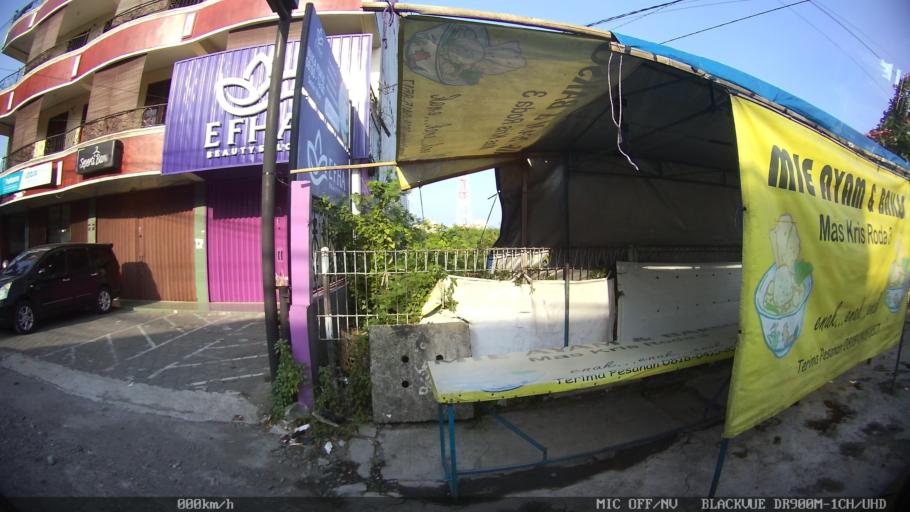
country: ID
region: Daerah Istimewa Yogyakarta
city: Depok
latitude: -7.7708
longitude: 110.4051
